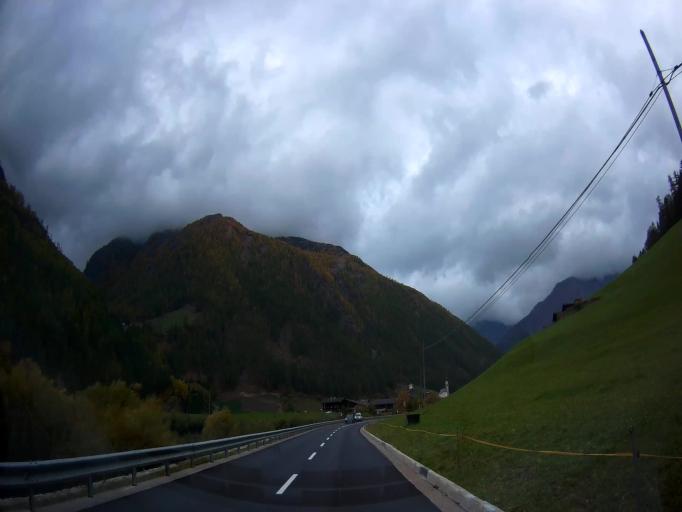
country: IT
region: Trentino-Alto Adige
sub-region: Bolzano
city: Senales
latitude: 46.7184
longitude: 10.8674
